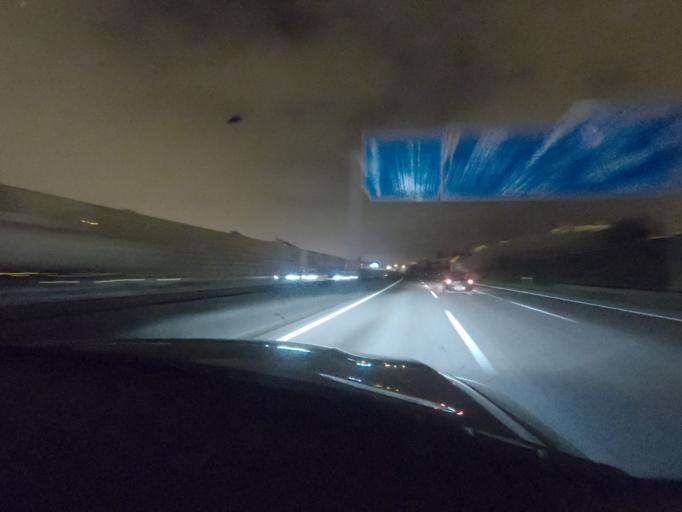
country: PT
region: Lisbon
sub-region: Vila Franca de Xira
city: Sobralinho
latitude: 38.9047
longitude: -9.0407
